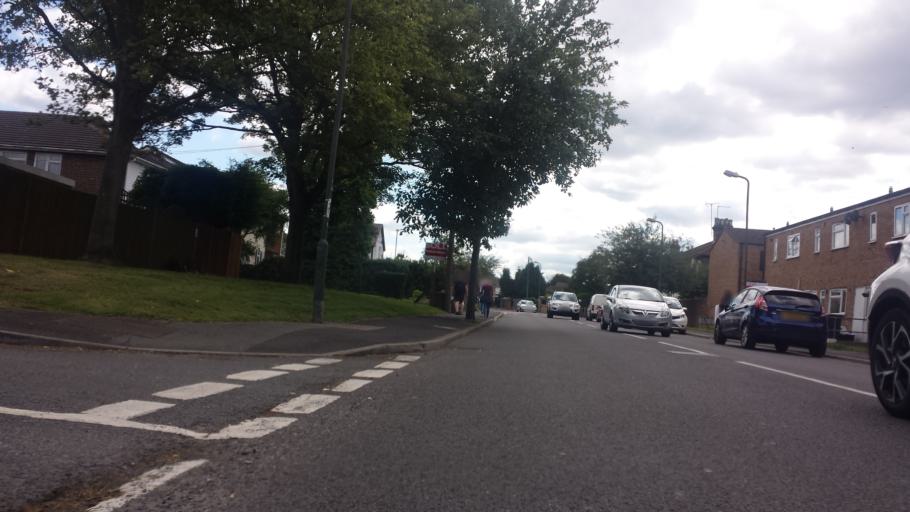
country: GB
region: England
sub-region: Greater London
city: Sidcup
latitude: 51.3997
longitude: 0.1160
